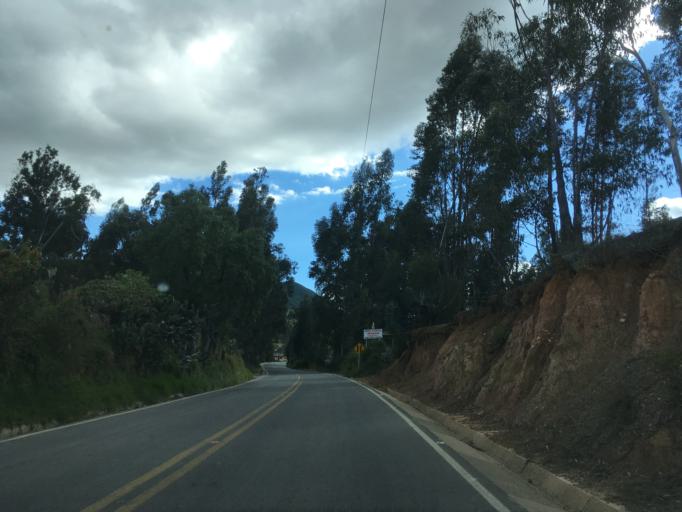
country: CO
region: Boyaca
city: Firavitoba
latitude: 5.6226
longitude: -73.0107
